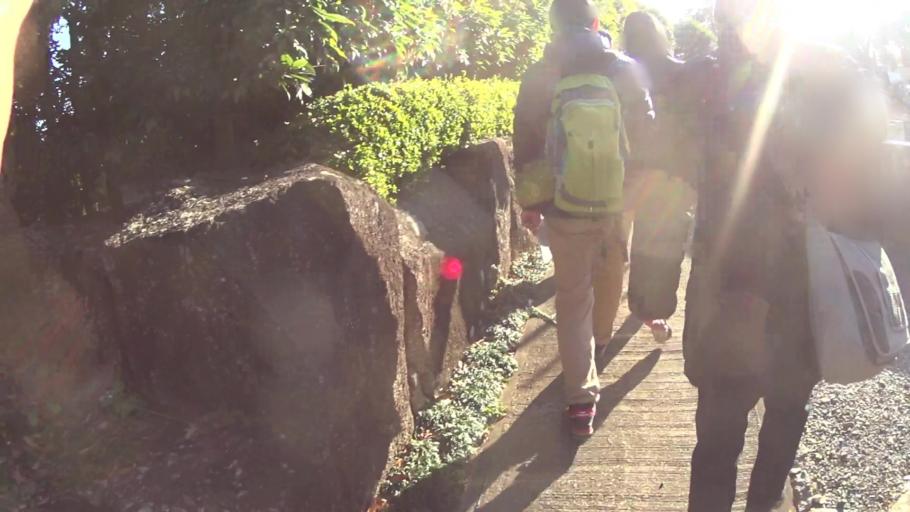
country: JP
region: Saitama
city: Shimotoda
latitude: 35.8419
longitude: 139.6901
